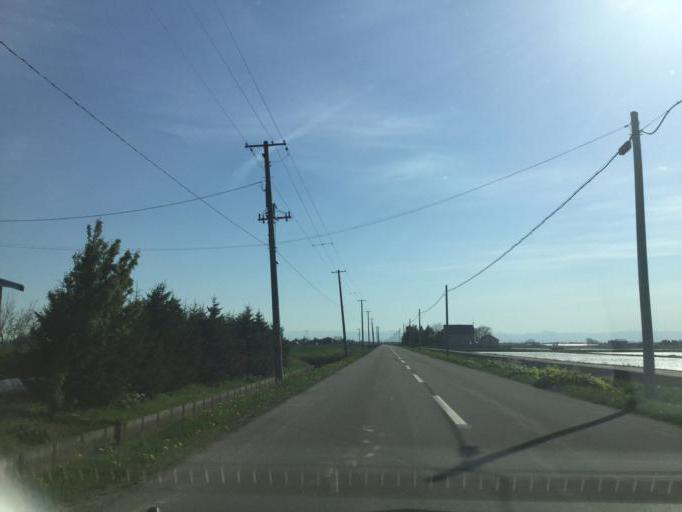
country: JP
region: Hokkaido
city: Iwamizawa
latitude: 43.1659
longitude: 141.7328
